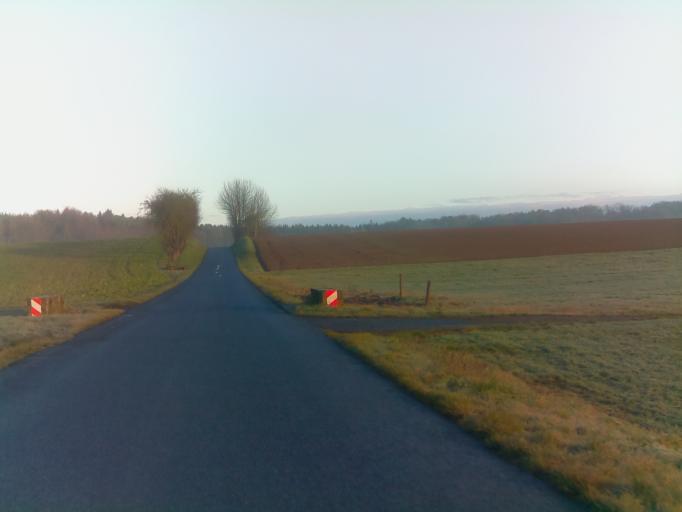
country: DE
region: Bavaria
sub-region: Regierungsbezirk Unterfranken
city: Neunkirchen
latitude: 49.7166
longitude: 9.3935
